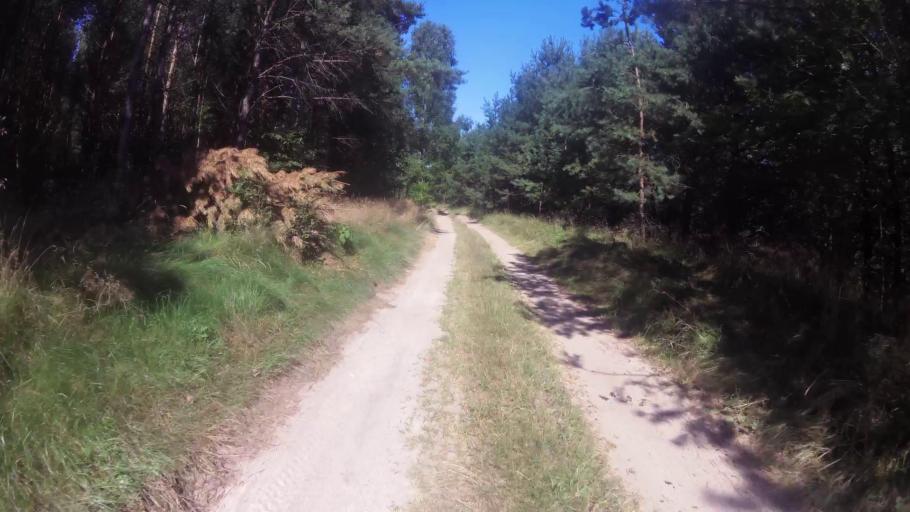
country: PL
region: West Pomeranian Voivodeship
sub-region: Powiat stargardzki
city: Insko
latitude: 53.4417
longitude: 15.6232
